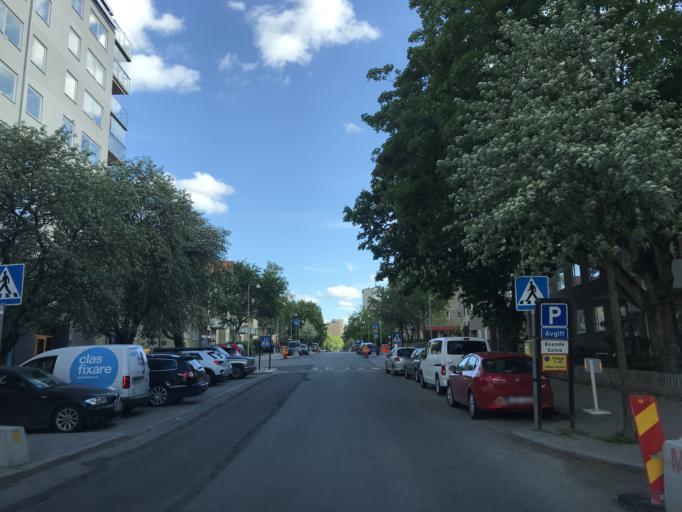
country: SE
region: Stockholm
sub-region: Solna Kommun
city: Solna
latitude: 59.3531
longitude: 17.9969
